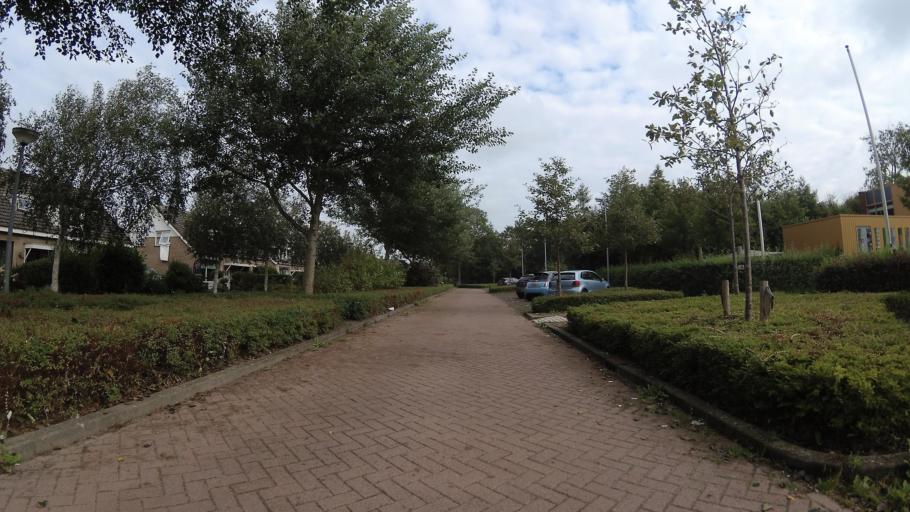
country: NL
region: North Holland
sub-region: Gemeente Schagen
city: Schagen
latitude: 52.8355
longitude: 4.8657
